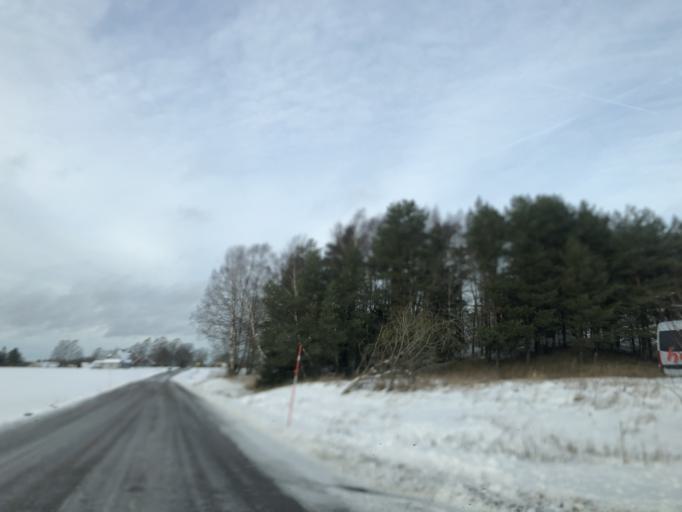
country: SE
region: Vaestra Goetaland
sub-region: Ulricehamns Kommun
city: Ulricehamn
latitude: 57.8154
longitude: 13.5340
